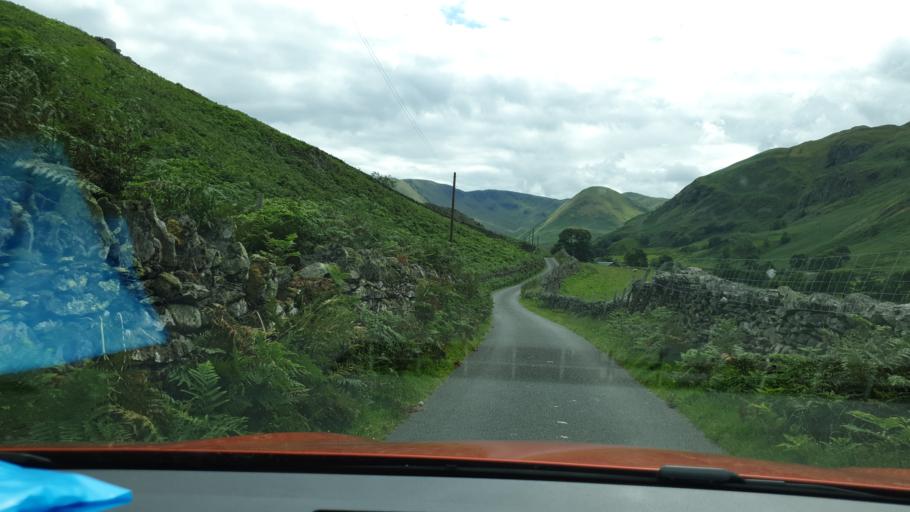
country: GB
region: England
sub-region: Cumbria
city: Ambleside
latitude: 54.5615
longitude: -2.8765
